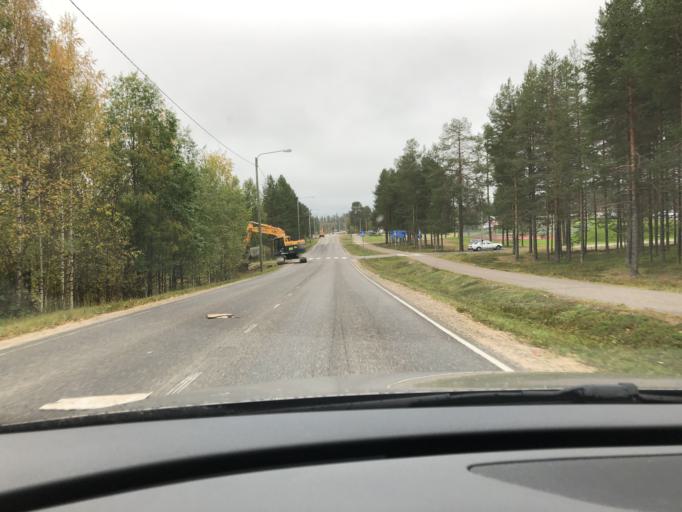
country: FI
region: Lapland
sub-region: Itae-Lappi
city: Posio
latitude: 66.1117
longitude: 28.1798
